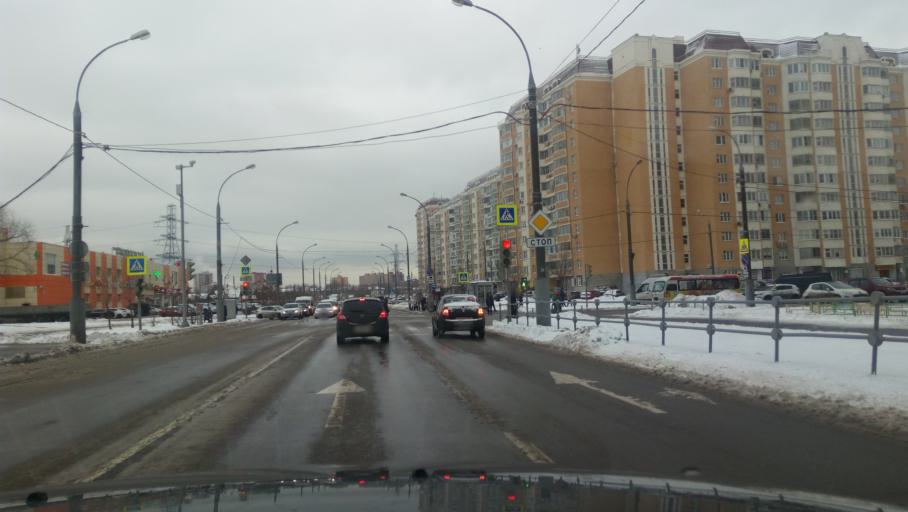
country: RU
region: Moscow
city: Nekrasovka
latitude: 55.7130
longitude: 37.8982
